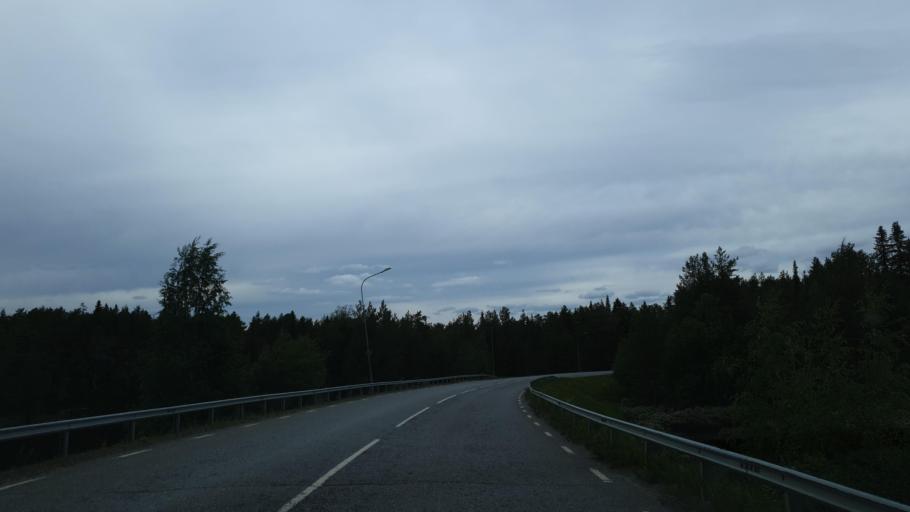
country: SE
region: Vaesterbotten
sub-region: Sorsele Kommun
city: Sorsele
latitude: 65.5439
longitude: 17.5088
